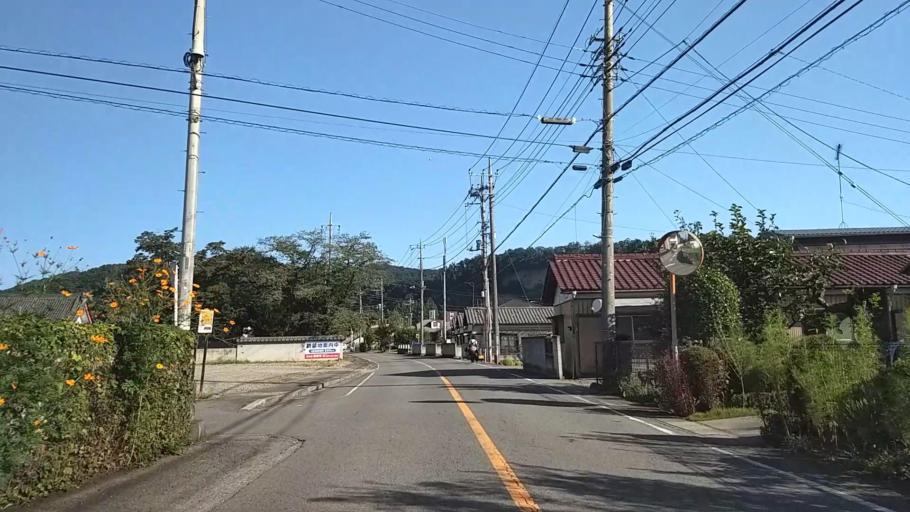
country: JP
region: Gunma
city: Annaka
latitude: 36.3342
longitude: 138.9212
